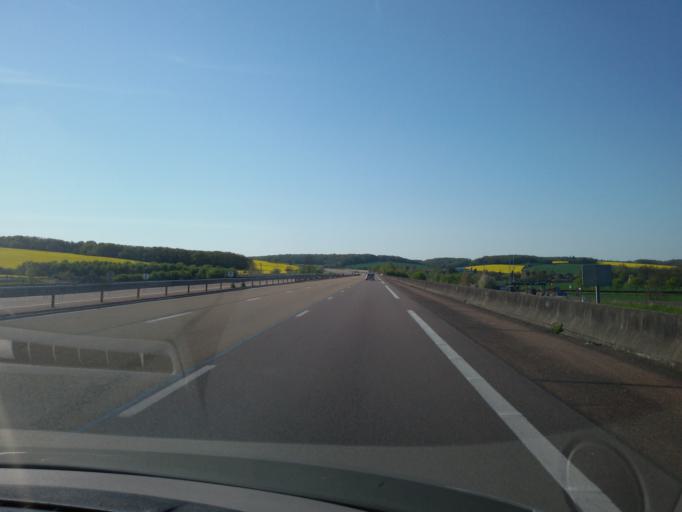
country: FR
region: Bourgogne
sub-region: Departement de l'Yonne
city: Saint-Julien-du-Sault
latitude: 47.9421
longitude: 3.2416
